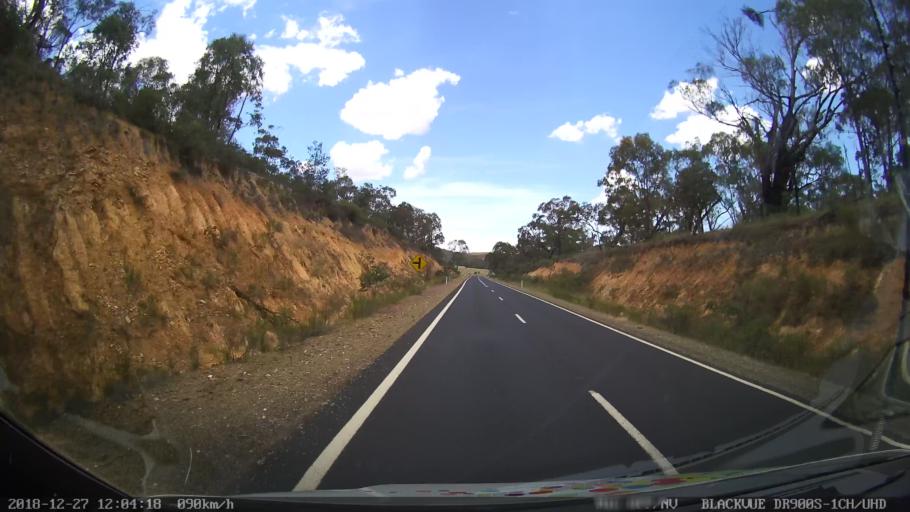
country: AU
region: New South Wales
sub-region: Blayney
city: Blayney
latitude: -33.7957
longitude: 149.3520
